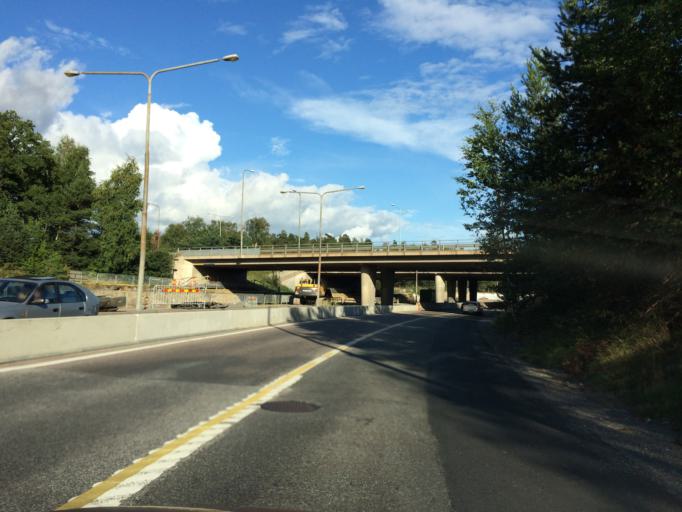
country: SE
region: Stockholm
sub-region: Huddinge Kommun
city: Segeltorp
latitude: 59.2767
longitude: 17.9136
